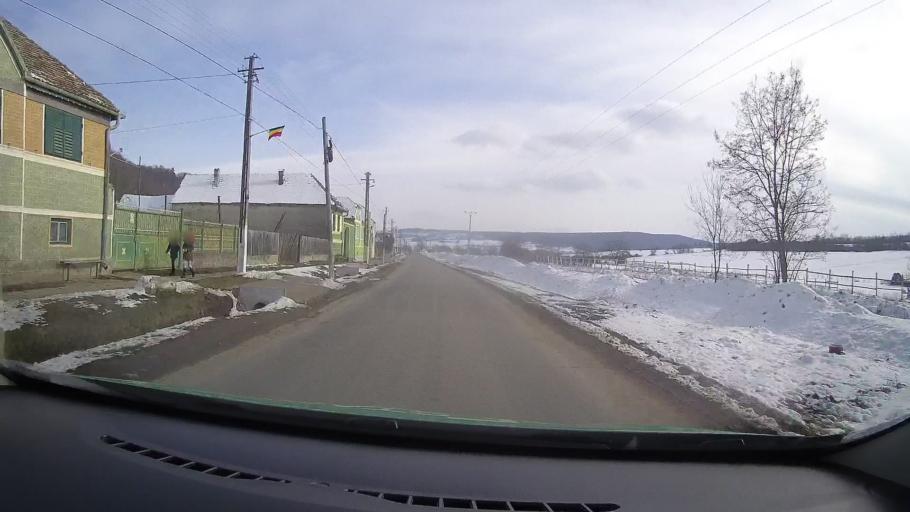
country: RO
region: Sibiu
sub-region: Comuna Iacobeni
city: Iacobeni
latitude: 46.0480
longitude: 24.7216
